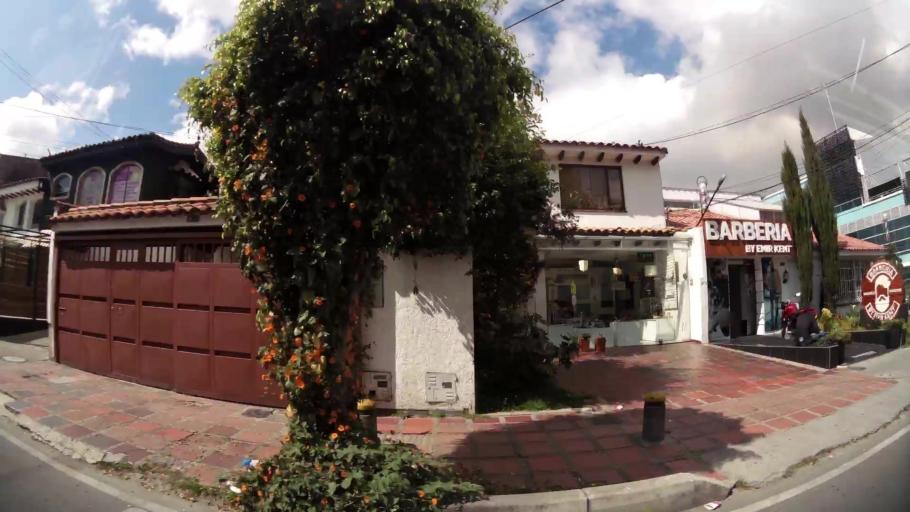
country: CO
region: Bogota D.C.
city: Barrio San Luis
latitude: 4.6920
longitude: -74.0437
